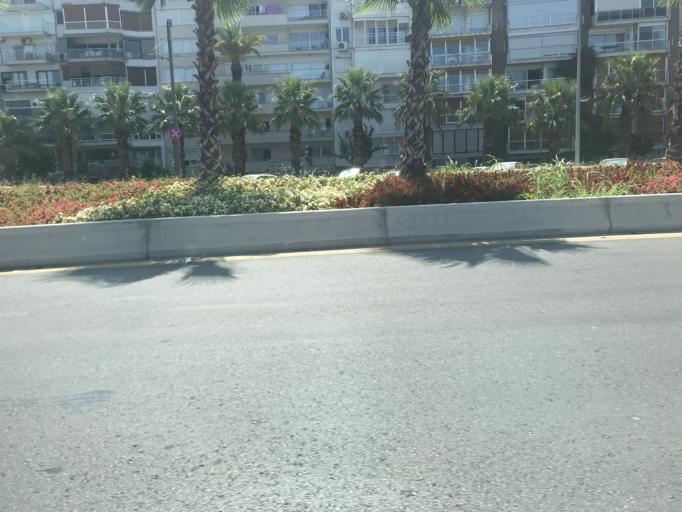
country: TR
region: Izmir
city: Izmir
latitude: 38.4028
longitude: 27.0949
